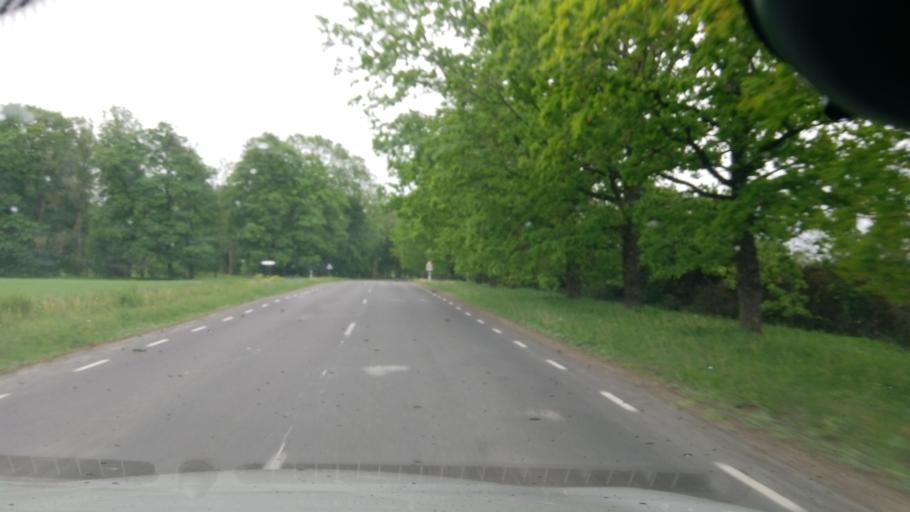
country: EE
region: Jaervamaa
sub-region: Paide linn
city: Paide
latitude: 58.8930
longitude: 25.7130
